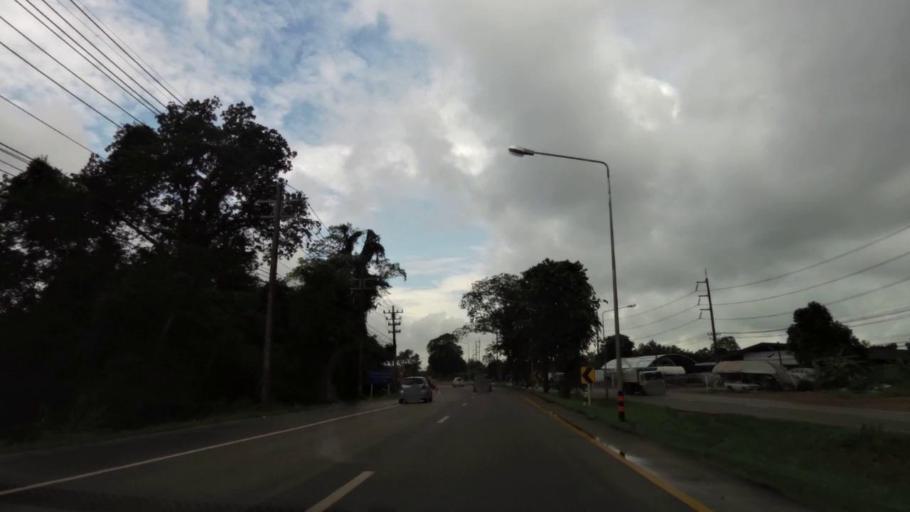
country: TH
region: Chanthaburi
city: Khlung
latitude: 12.4829
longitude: 102.1812
